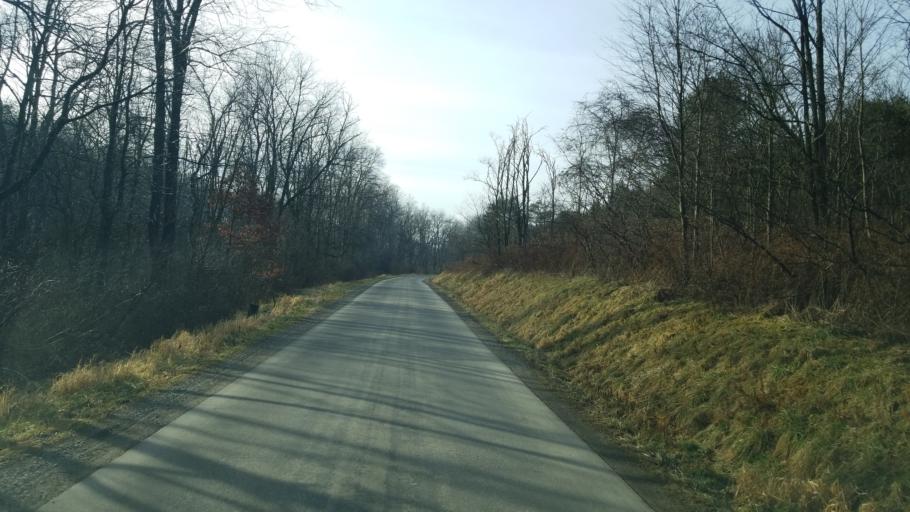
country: US
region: Pennsylvania
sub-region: Indiana County
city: Chevy Chase Heights
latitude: 40.8040
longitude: -79.1684
